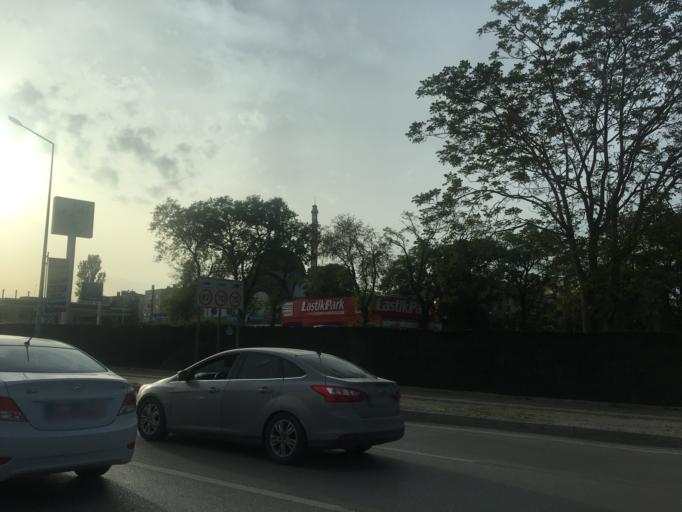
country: TR
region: Bursa
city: Yildirim
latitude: 40.2129
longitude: 29.0019
